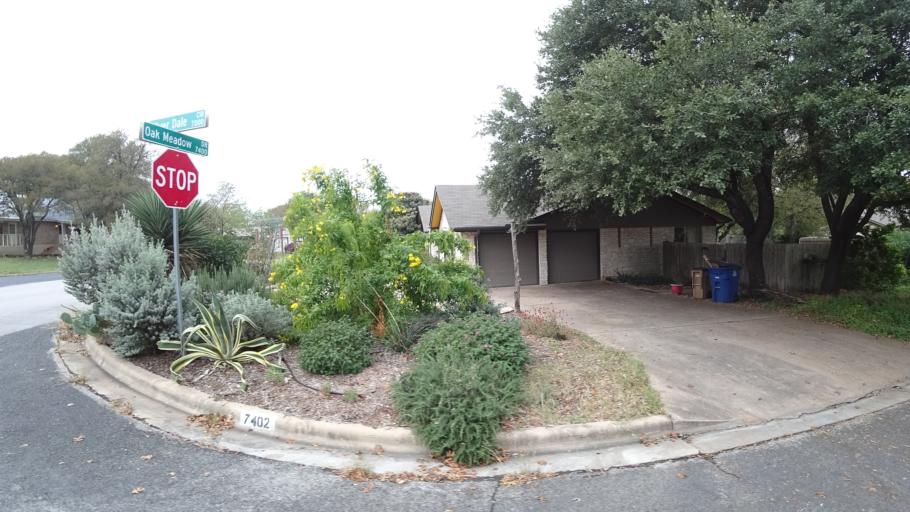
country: US
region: Texas
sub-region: Travis County
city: Barton Creek
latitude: 30.2349
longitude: -97.8812
